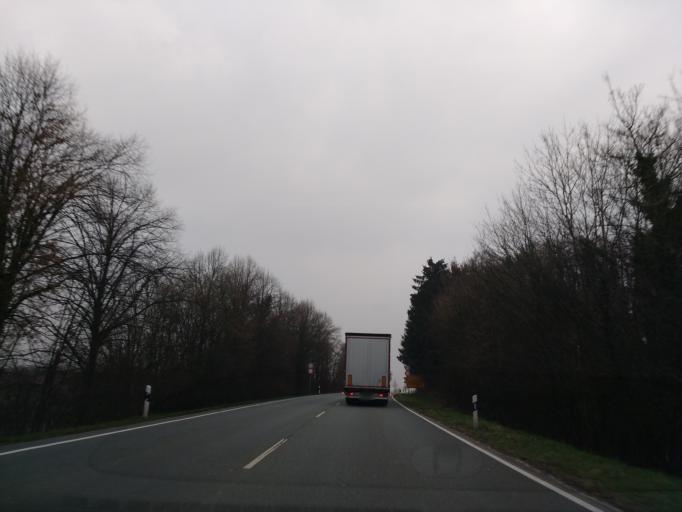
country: DE
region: North Rhine-Westphalia
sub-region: Regierungsbezirk Munster
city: Lotte
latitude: 52.2743
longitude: 7.8953
